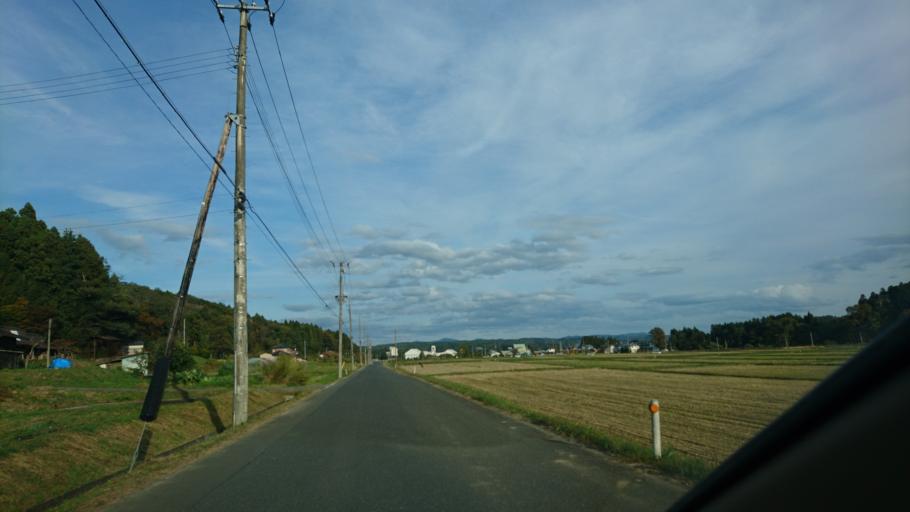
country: JP
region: Iwate
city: Ichinoseki
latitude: 38.8449
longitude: 141.1493
